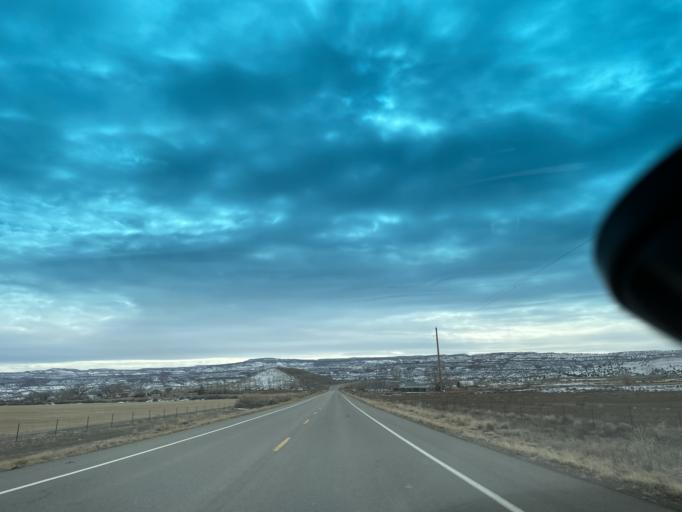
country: US
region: Colorado
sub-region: Mesa County
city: Loma
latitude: 39.1859
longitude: -108.8129
